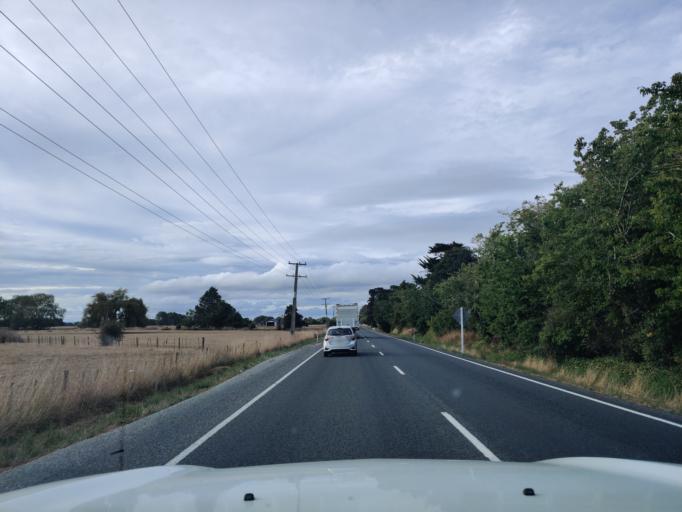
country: NZ
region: Waikato
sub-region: Hamilton City
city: Hamilton
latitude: -37.6929
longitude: 175.3382
